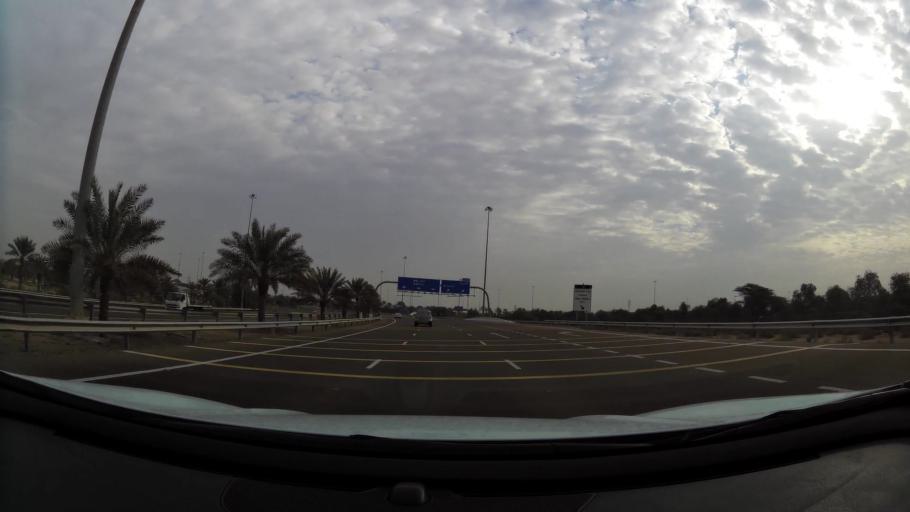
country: AE
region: Abu Dhabi
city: Al Ain
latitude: 24.1731
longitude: 55.1322
